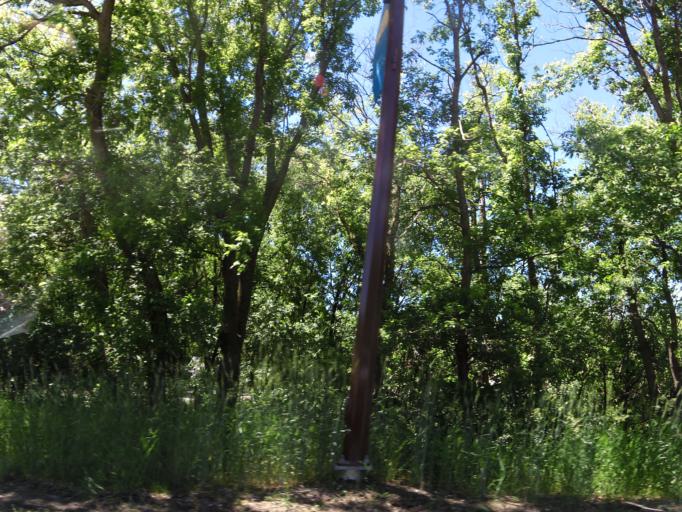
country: US
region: Minnesota
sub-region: Becker County
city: Detroit Lakes
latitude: 46.8248
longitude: -95.8499
